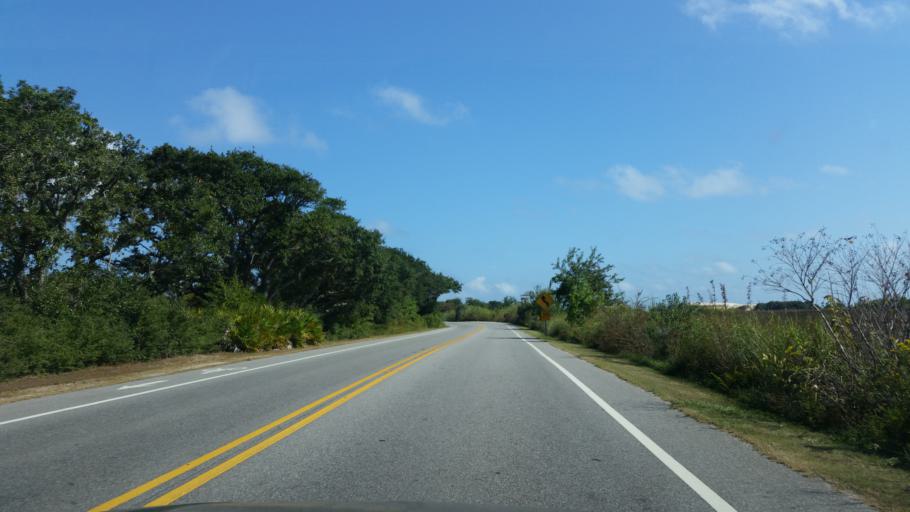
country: US
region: Alabama
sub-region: Baldwin County
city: Gulf Shores
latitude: 30.2550
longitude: -87.6703
